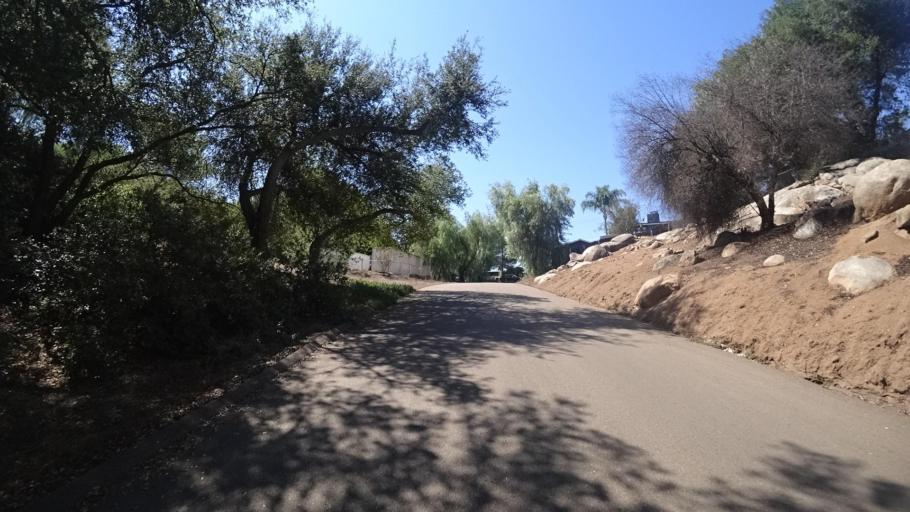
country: US
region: California
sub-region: San Diego County
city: Crest
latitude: 32.8088
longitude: -116.8628
